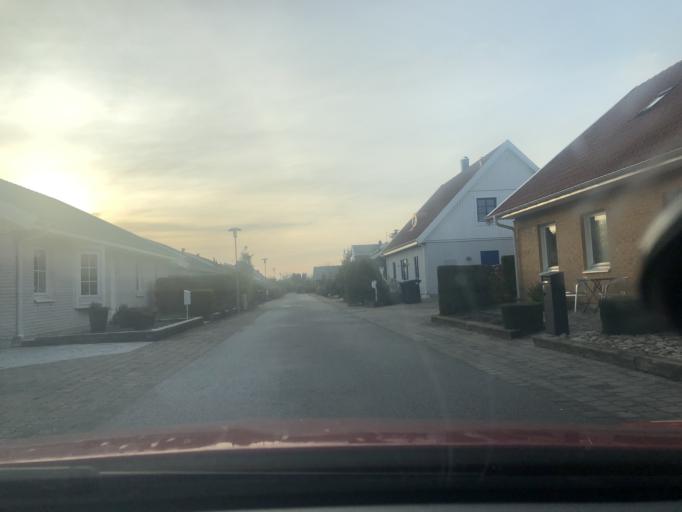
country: SE
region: Skane
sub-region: Burlovs Kommun
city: Arloev
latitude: 55.6047
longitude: 13.0912
